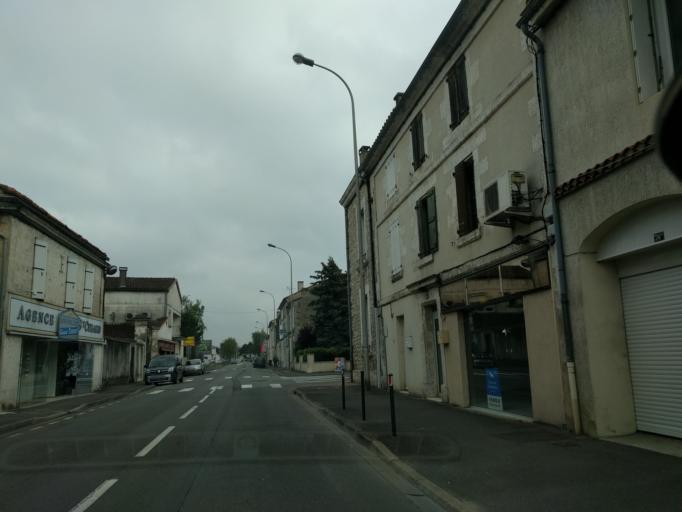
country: FR
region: Poitou-Charentes
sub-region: Departement de la Charente
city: Angouleme
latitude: 45.6579
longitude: 0.1458
